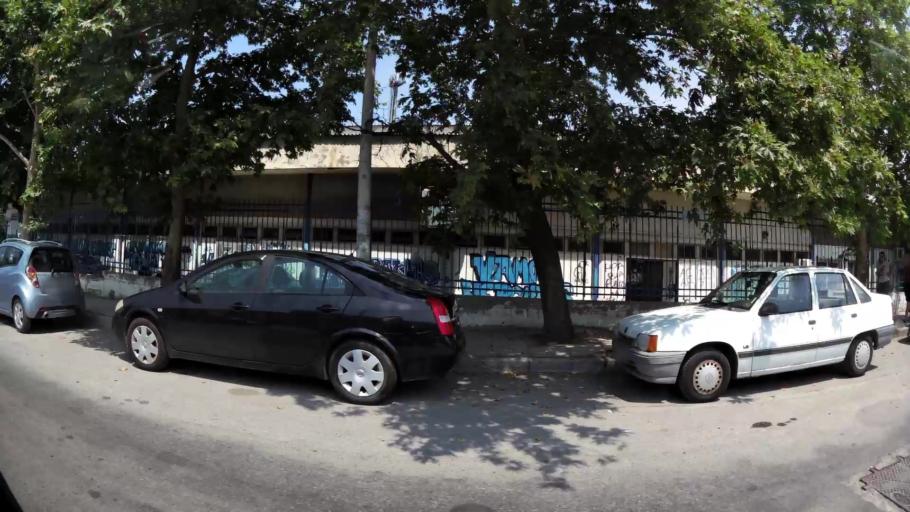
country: GR
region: Central Macedonia
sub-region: Nomos Thessalonikis
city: Agios Pavlos
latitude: 40.6278
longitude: 22.9643
